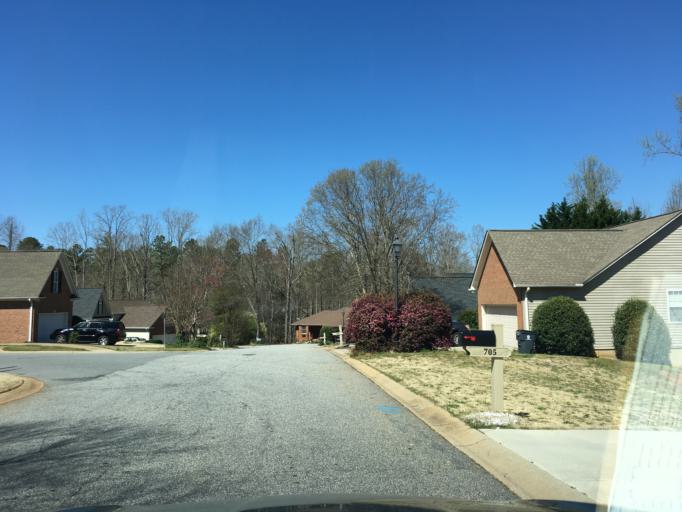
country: US
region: South Carolina
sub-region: Spartanburg County
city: Roebuck
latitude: 34.8815
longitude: -82.0410
